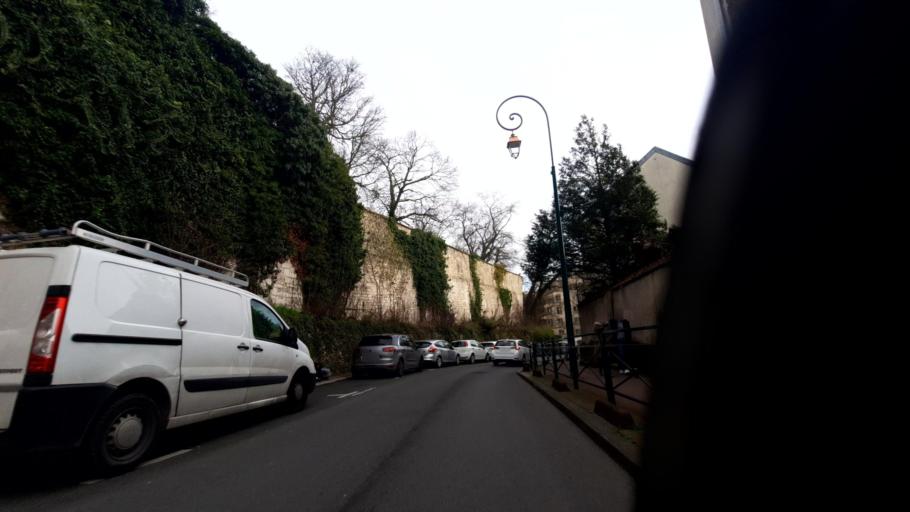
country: FR
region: Ile-de-France
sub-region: Departement du Val-de-Marne
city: Saint-Maurice
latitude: 48.8193
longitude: 2.4238
